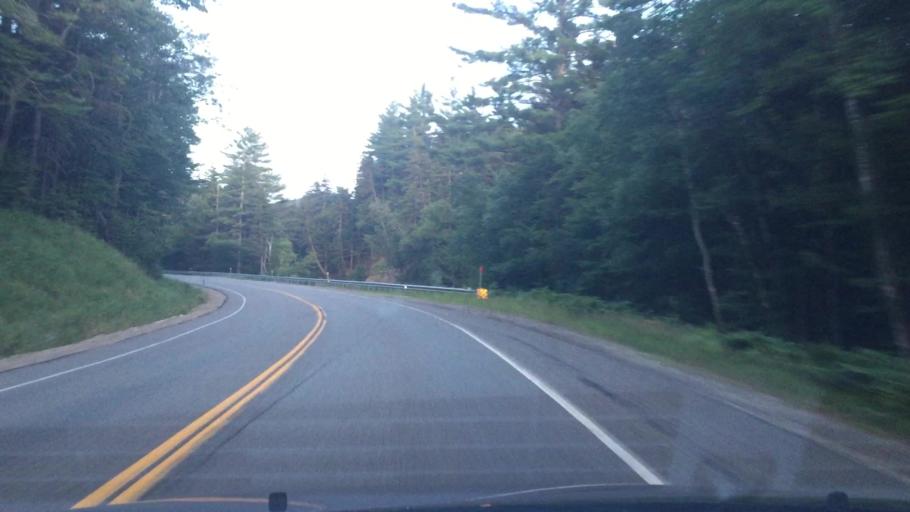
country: US
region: New Hampshire
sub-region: Grafton County
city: Woodstock
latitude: 44.0384
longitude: -71.5387
